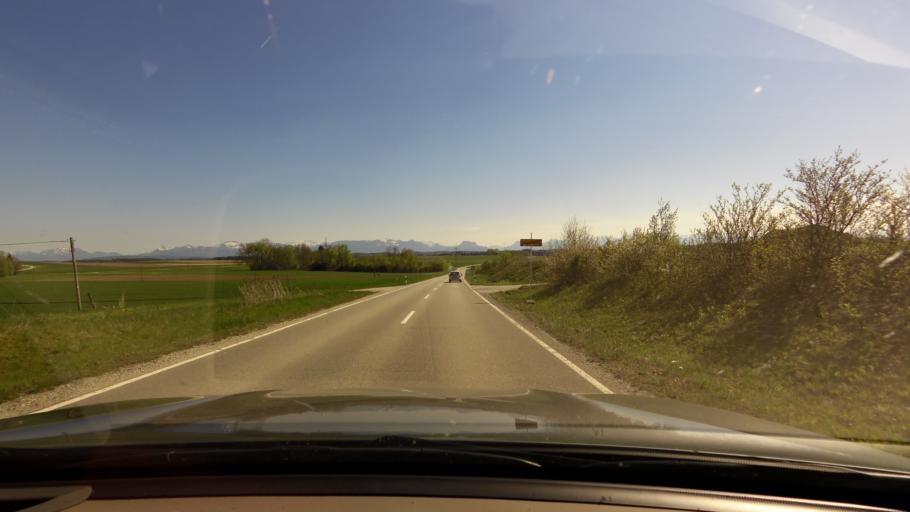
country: DE
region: Bavaria
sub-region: Upper Bavaria
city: Griesstatt
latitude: 47.9822
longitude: 12.1769
